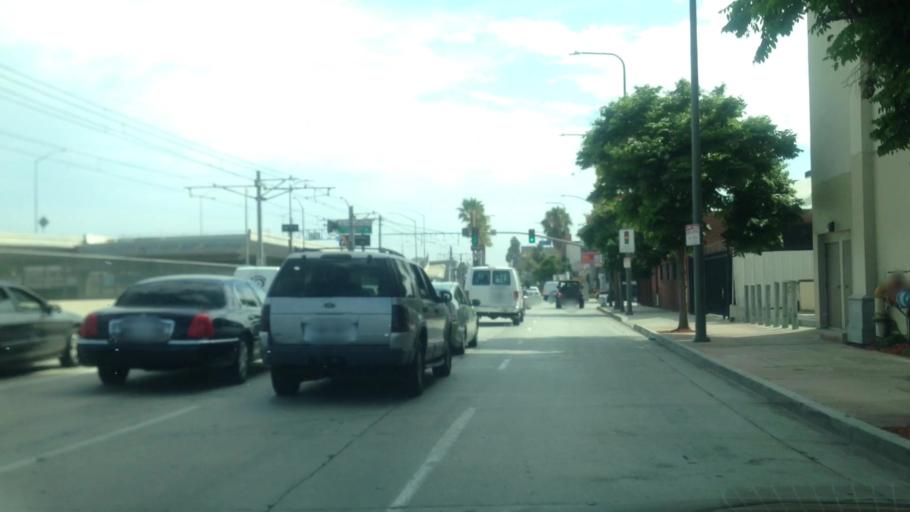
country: US
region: California
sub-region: Los Angeles County
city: Los Angeles
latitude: 34.0267
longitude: -118.2754
